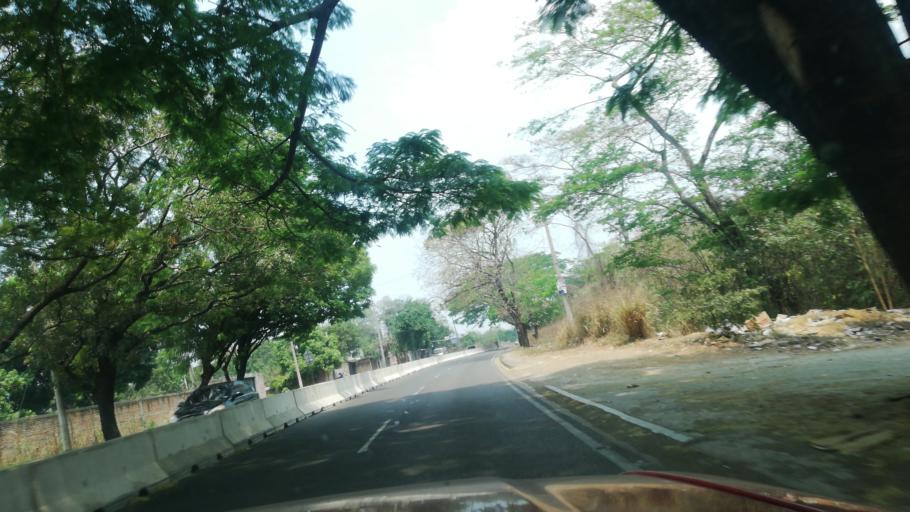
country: SV
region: Santa Ana
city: Santa Ana
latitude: 13.9772
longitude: -89.5923
